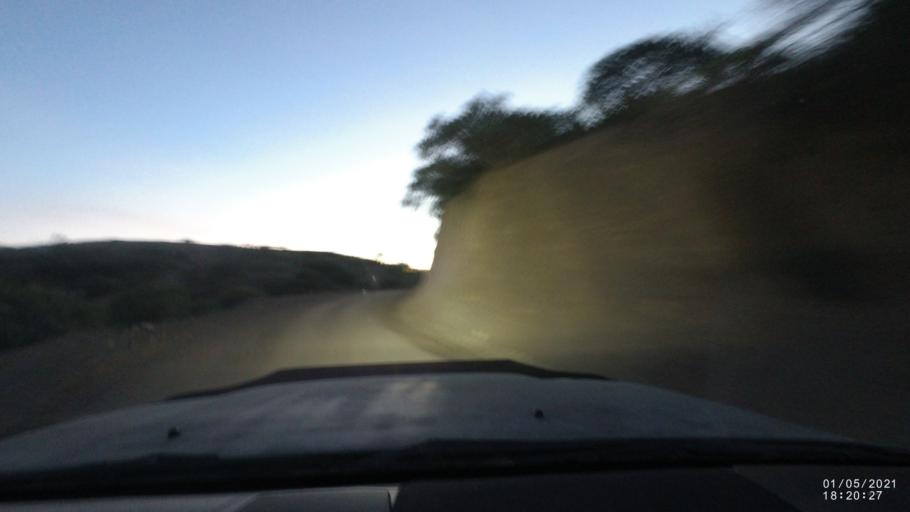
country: BO
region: Cochabamba
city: Capinota
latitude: -17.6606
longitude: -66.2279
